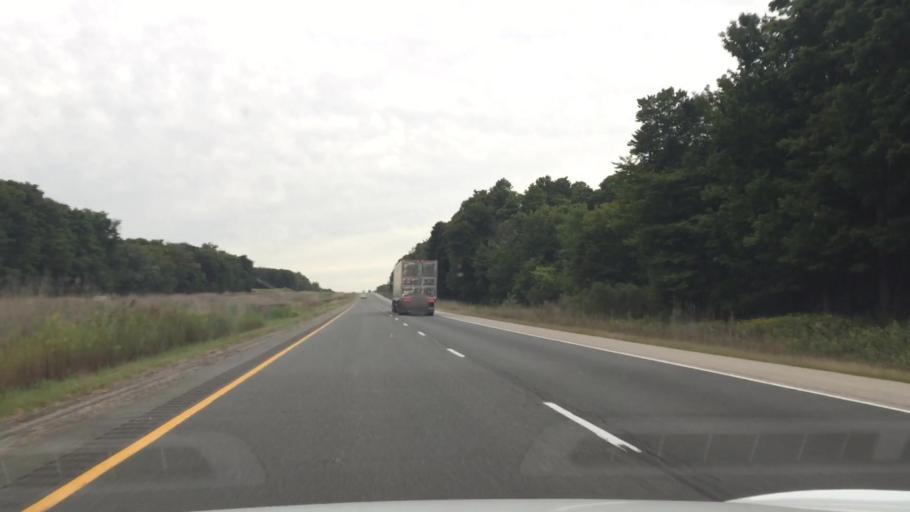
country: CA
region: Ontario
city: Lambton Shores
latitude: 42.9924
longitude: -81.7970
